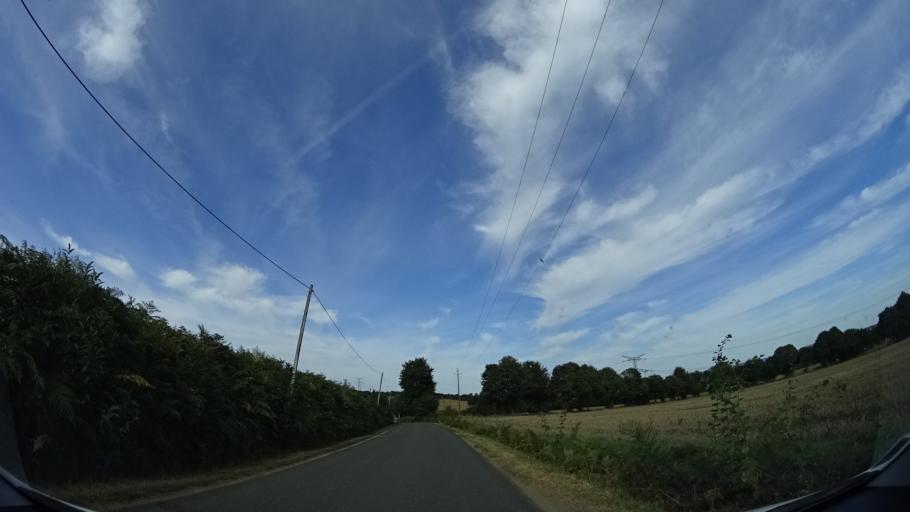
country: FR
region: Brittany
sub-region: Departement d'Ille-et-Vilaine
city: Romagne
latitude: 48.3244
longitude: -1.2683
